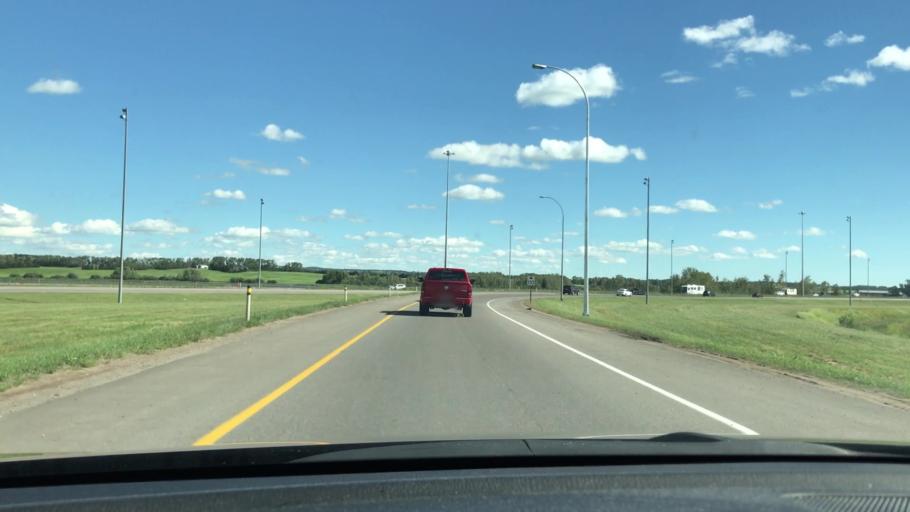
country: CA
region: Alberta
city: Red Deer
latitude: 52.1990
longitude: -113.8166
